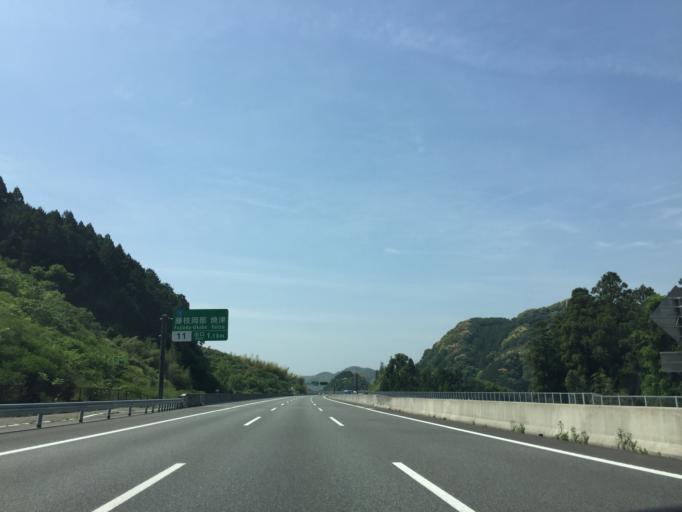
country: JP
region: Shizuoka
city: Fujieda
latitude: 34.9315
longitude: 138.2755
